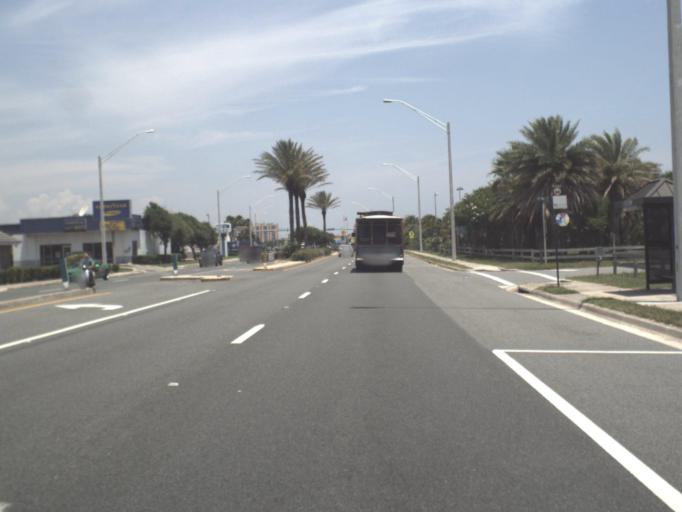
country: US
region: Florida
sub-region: Duval County
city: Jacksonville Beach
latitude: 30.2707
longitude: -81.3885
